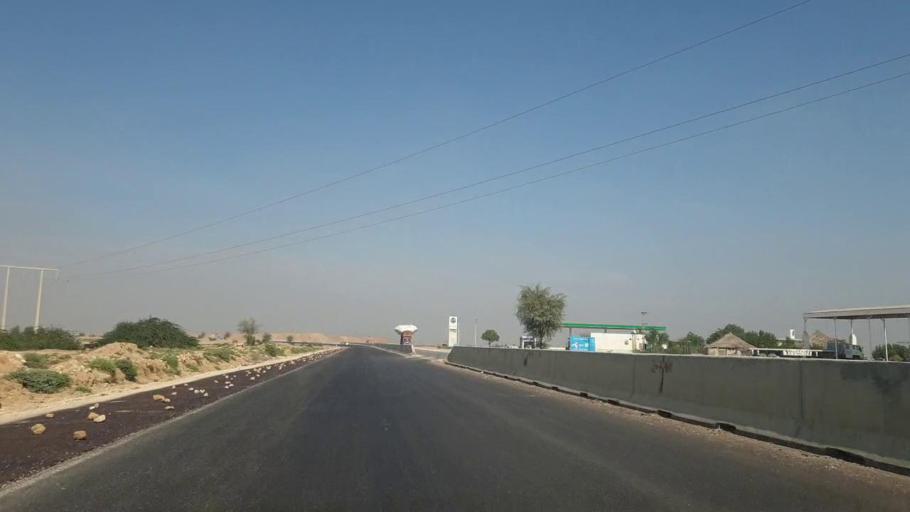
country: PK
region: Sindh
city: Jamshoro
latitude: 25.5699
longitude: 68.3136
